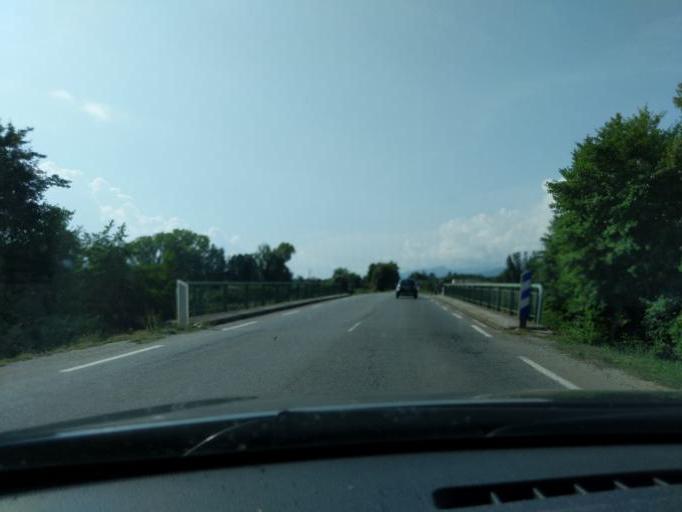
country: FR
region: Corsica
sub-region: Departement de la Haute-Corse
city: Ghisonaccia
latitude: 41.9763
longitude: 9.3995
